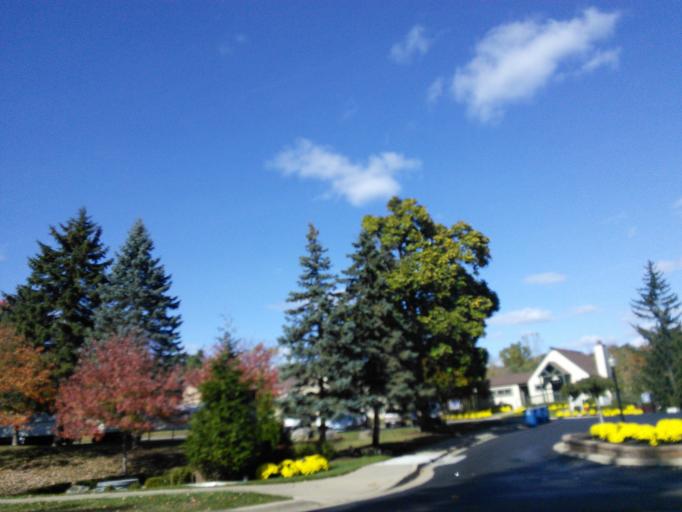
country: US
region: Michigan
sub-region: Washtenaw County
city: Ann Arbor
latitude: 42.2750
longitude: -83.7725
